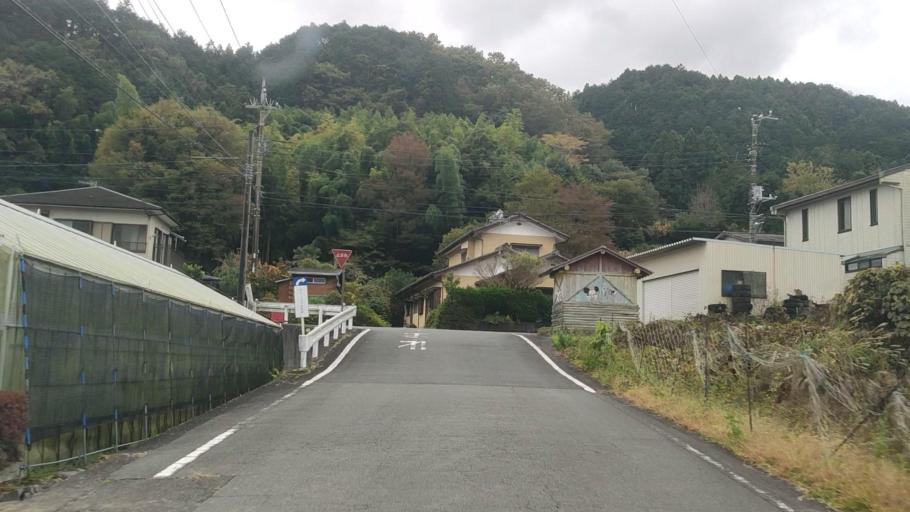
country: JP
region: Shizuoka
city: Ito
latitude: 34.9149
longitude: 138.9784
